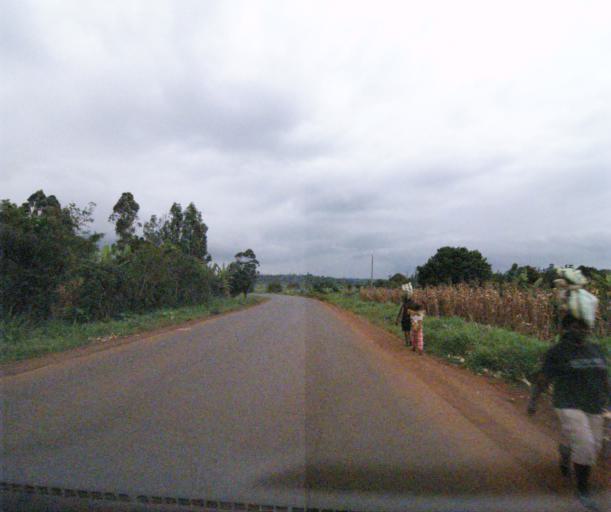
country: CM
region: West
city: Bansoa
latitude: 5.4854
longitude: 10.2178
